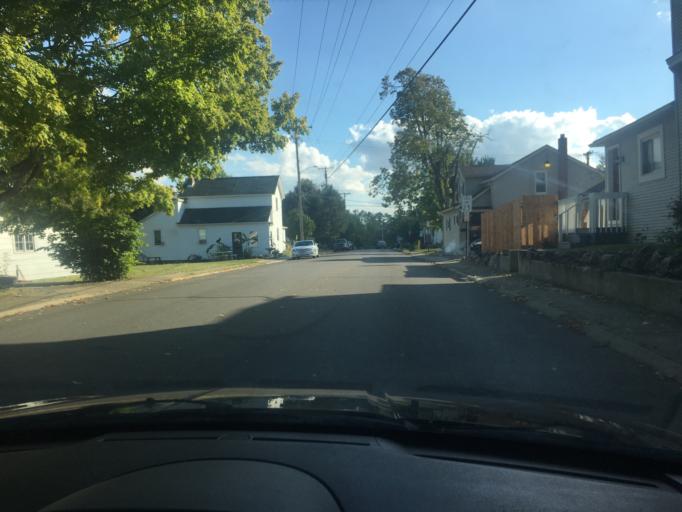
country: US
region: Ohio
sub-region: Logan County
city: Bellefontaine
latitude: 40.3604
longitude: -83.7488
